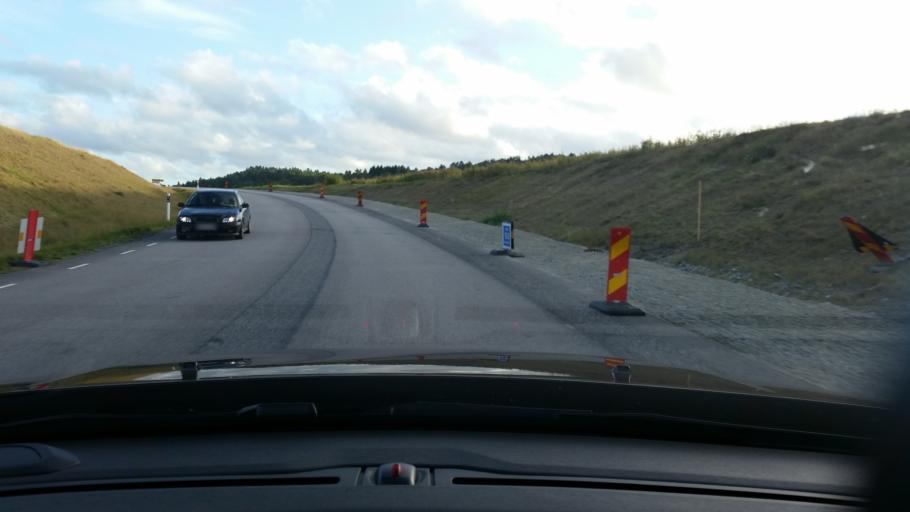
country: SE
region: Vaestra Goetaland
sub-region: Lilla Edets Kommun
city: Lodose
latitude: 58.0831
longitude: 12.1566
